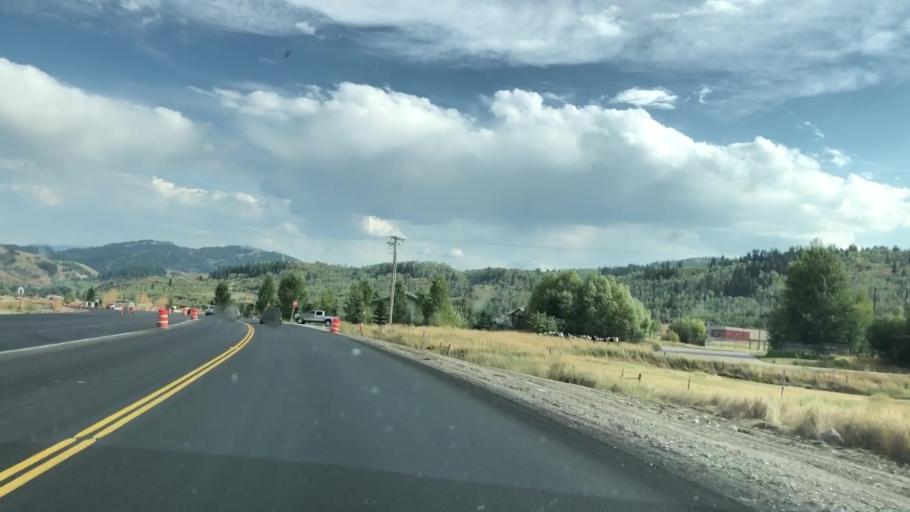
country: US
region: Wyoming
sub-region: Teton County
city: South Park
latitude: 43.3736
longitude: -110.7439
